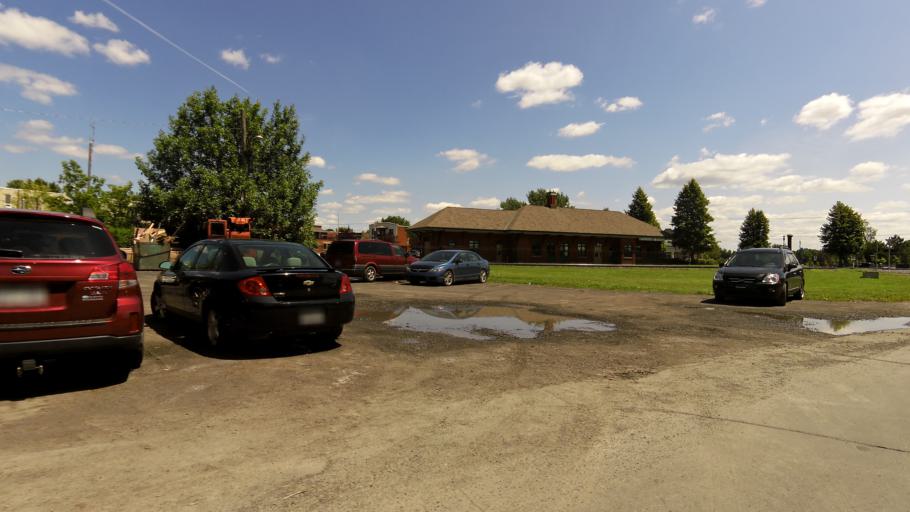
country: CA
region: Quebec
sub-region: Monteregie
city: Saint-Jean-sur-Richelieu
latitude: 45.3027
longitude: -73.2549
